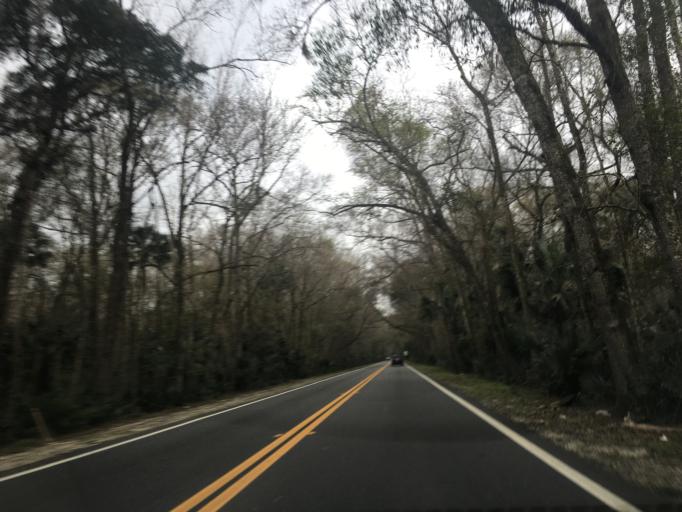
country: US
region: Florida
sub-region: Saint Johns County
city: Villano Beach
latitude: 29.9996
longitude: -81.4194
